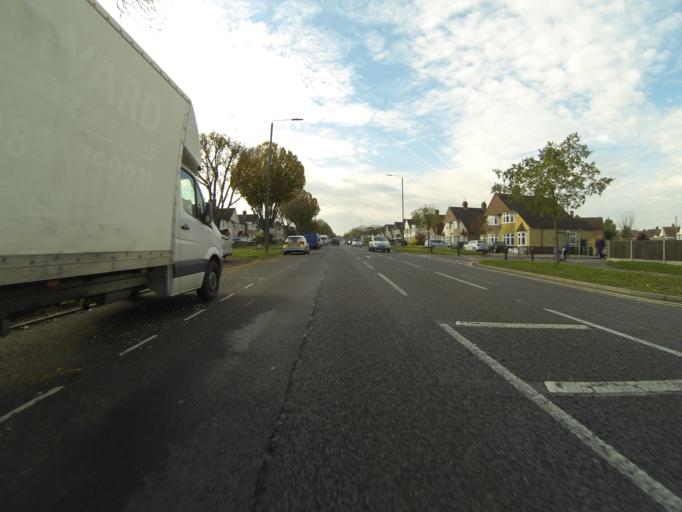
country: GB
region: England
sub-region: Greater London
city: Welling
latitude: 51.4638
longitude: 0.0934
